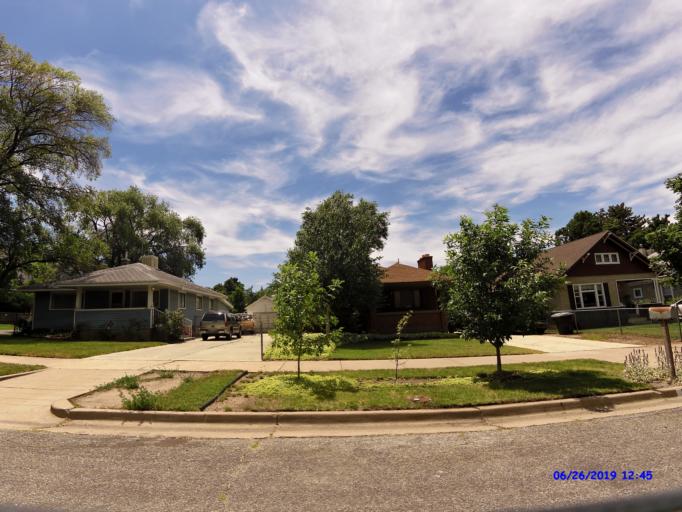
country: US
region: Utah
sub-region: Weber County
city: Ogden
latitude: 41.2287
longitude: -111.9513
